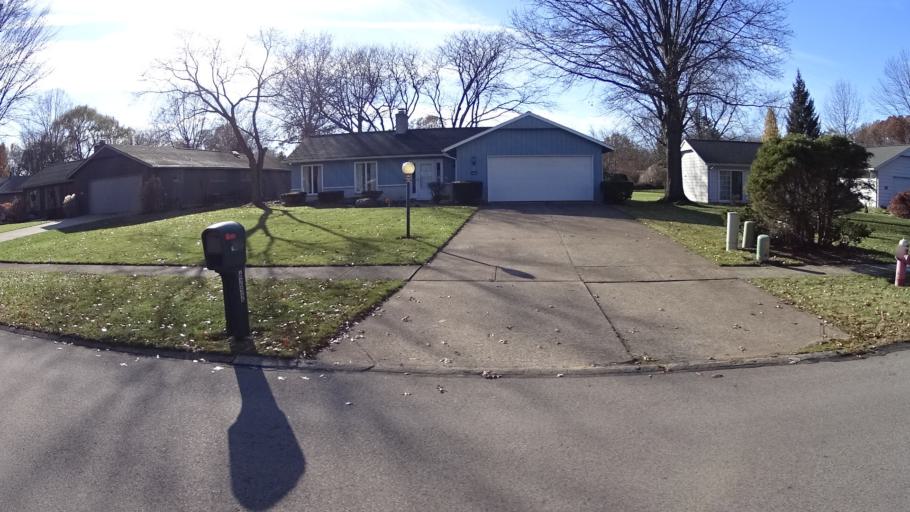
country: US
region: Ohio
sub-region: Lorain County
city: North Ridgeville
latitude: 41.3992
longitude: -81.9735
